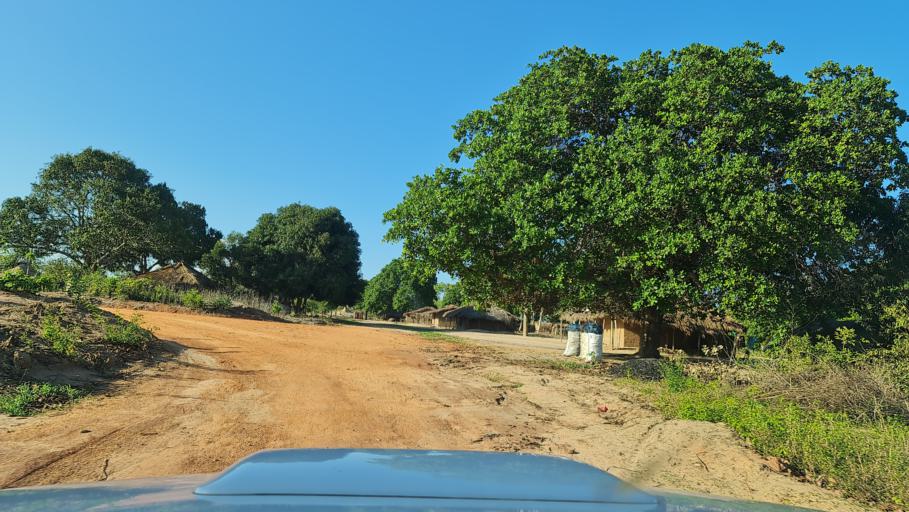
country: MZ
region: Nampula
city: Nacala
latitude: -14.6961
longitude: 40.3260
